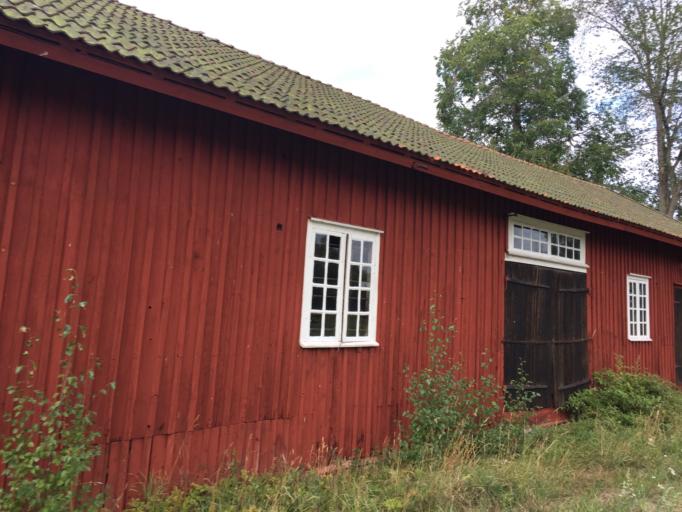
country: SE
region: Vaermland
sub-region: Filipstads Kommun
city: Lesjofors
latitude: 60.0253
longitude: 14.1101
